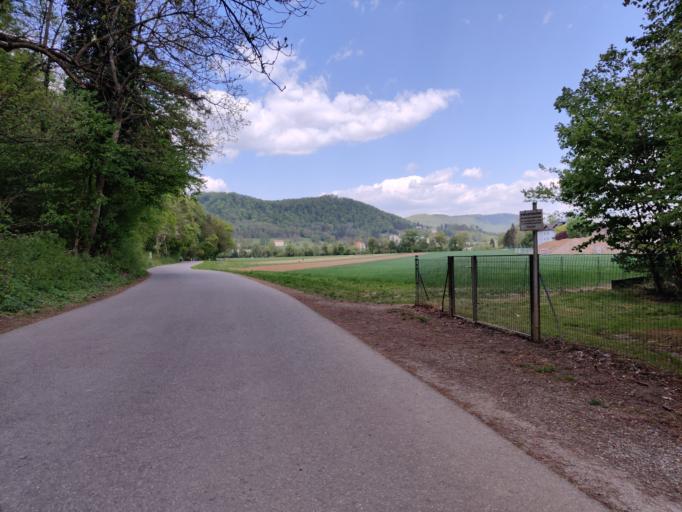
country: AT
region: Styria
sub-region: Graz Stadt
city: Wetzelsdorf
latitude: 47.0362
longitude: 15.3916
